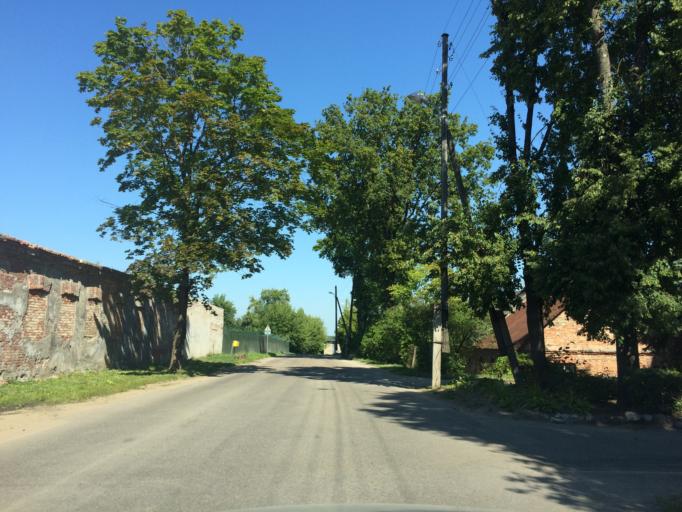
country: LV
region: Rezekne
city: Rezekne
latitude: 56.5049
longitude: 27.3196
